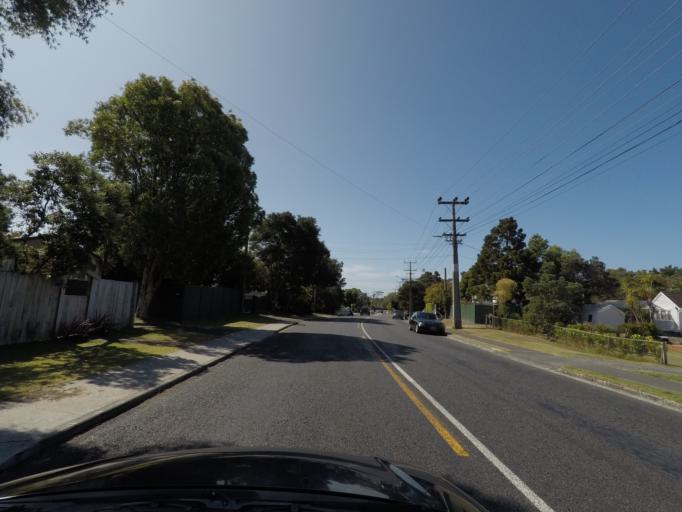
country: NZ
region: Auckland
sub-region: Auckland
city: Titirangi
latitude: -36.9287
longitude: 174.6548
